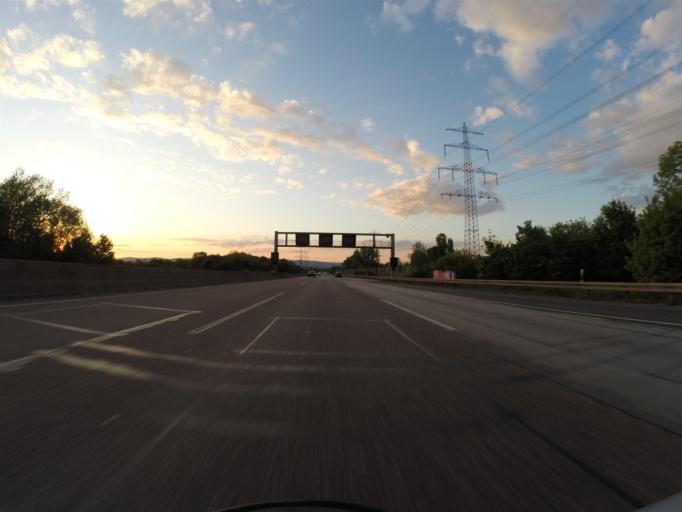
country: DE
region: Hesse
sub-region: Regierungsbezirk Darmstadt
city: Eschborn
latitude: 50.1147
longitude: 8.5990
